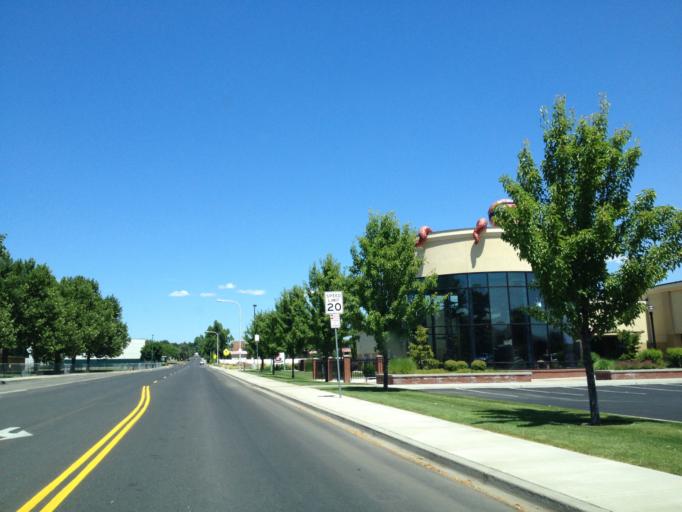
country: US
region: Washington
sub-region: Yakima County
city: West Valley
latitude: 46.5855
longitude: -120.5671
